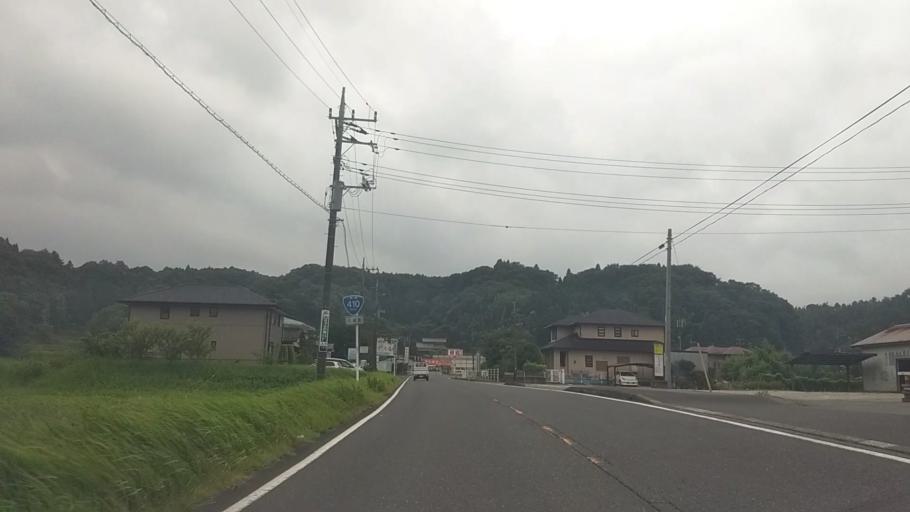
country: JP
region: Chiba
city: Kisarazu
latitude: 35.2879
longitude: 140.0832
